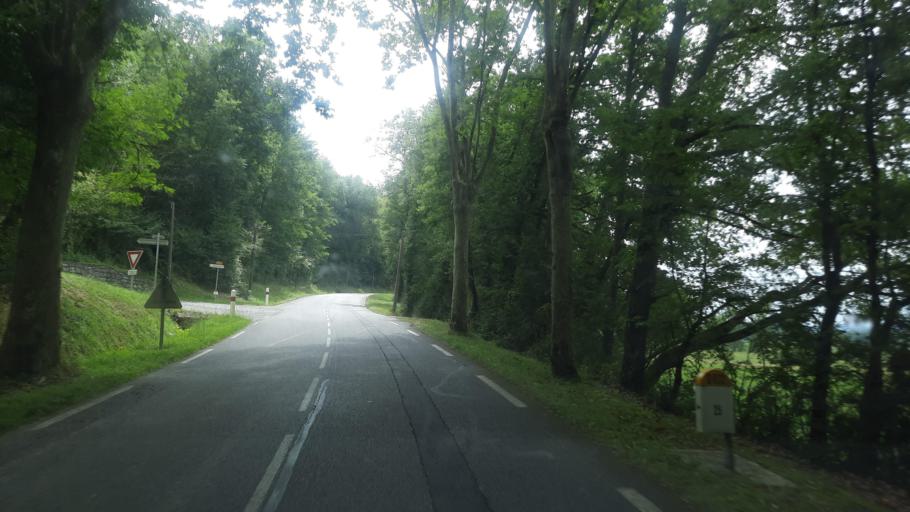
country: FR
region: Midi-Pyrenees
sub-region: Departement des Hautes-Pyrenees
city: Trie-sur-Baise
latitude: 43.3179
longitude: 0.3813
